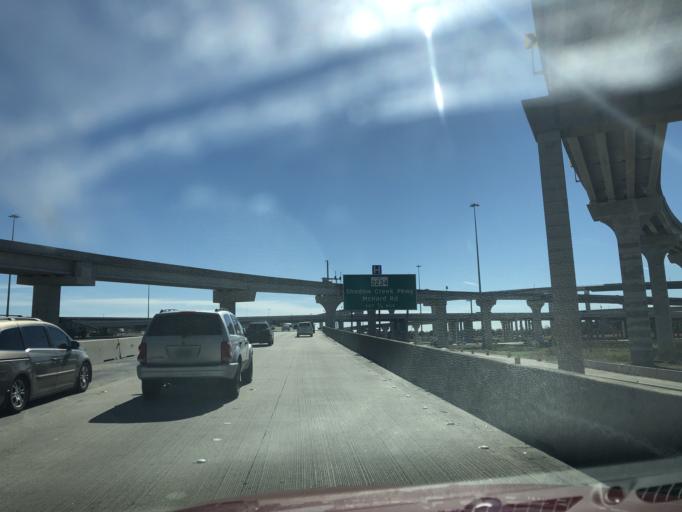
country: US
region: Texas
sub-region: Brazoria County
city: Brookside Village
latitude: 29.6003
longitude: -95.3870
